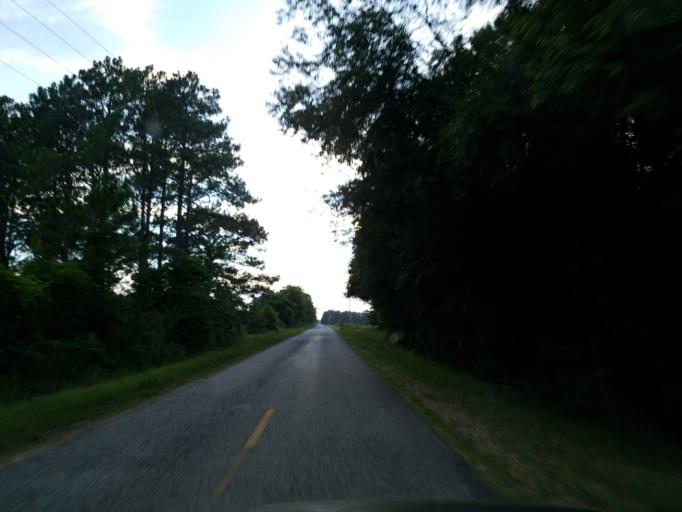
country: US
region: Georgia
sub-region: Crisp County
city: Cordele
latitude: 31.8350
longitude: -83.7778
